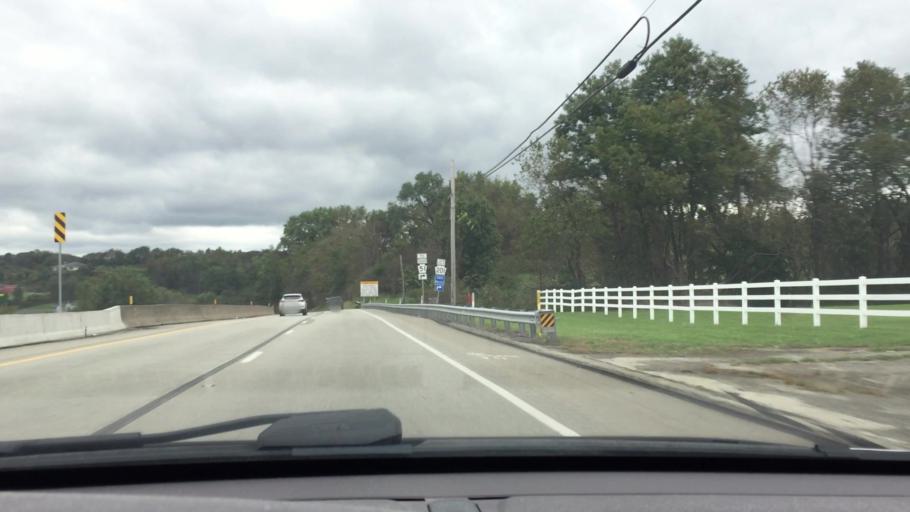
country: US
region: Pennsylvania
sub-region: Westmoreland County
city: Fellsburg
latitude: 40.1789
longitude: -79.8040
